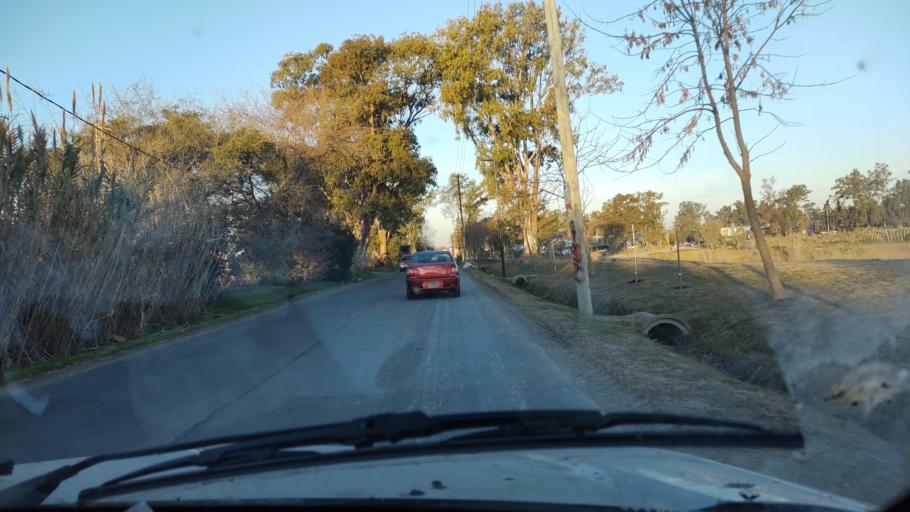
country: AR
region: Buenos Aires
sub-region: Partido de La Plata
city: La Plata
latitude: -34.9008
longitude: -58.0323
